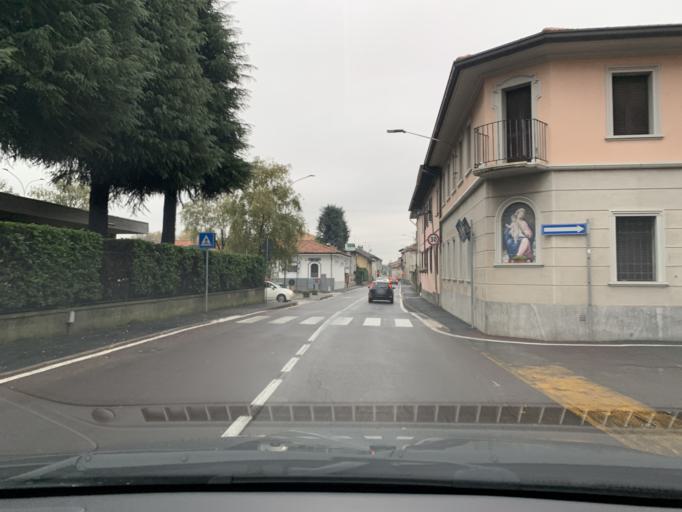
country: IT
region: Lombardy
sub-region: Provincia di Como
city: Rovello Porro
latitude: 45.6397
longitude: 9.0471
